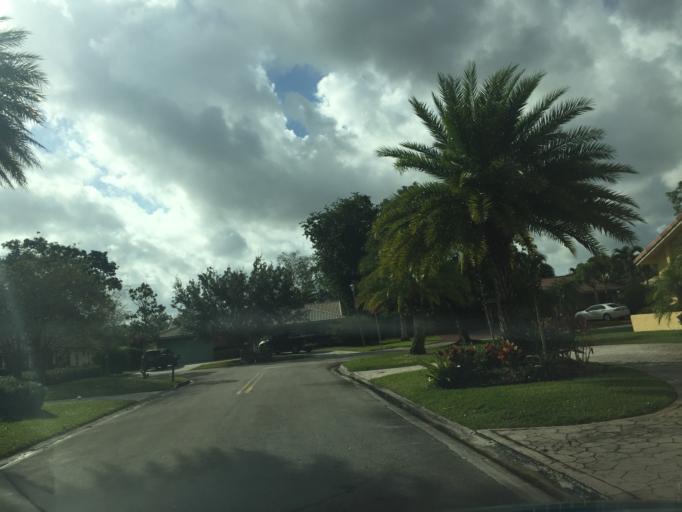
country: US
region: Florida
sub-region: Broward County
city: Tamarac
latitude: 26.2337
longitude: -80.2513
